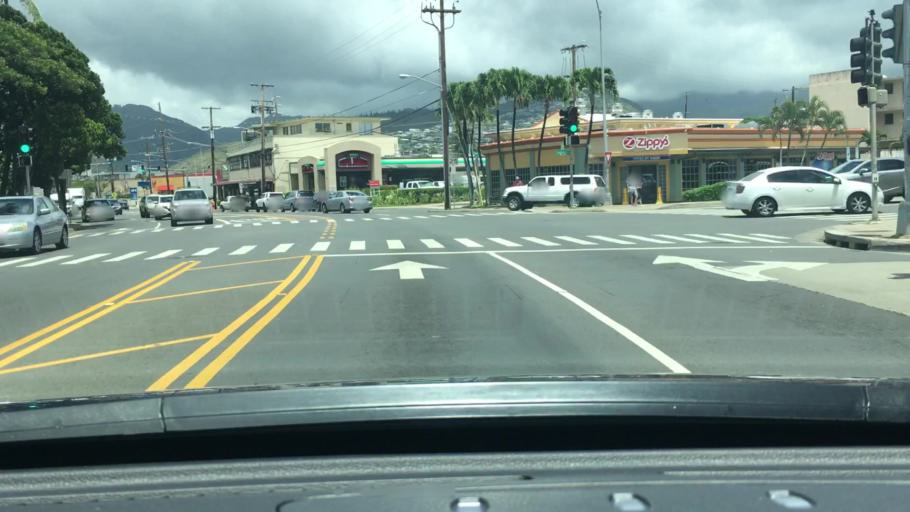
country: US
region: Hawaii
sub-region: Honolulu County
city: Honolulu
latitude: 21.2779
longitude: -157.8140
